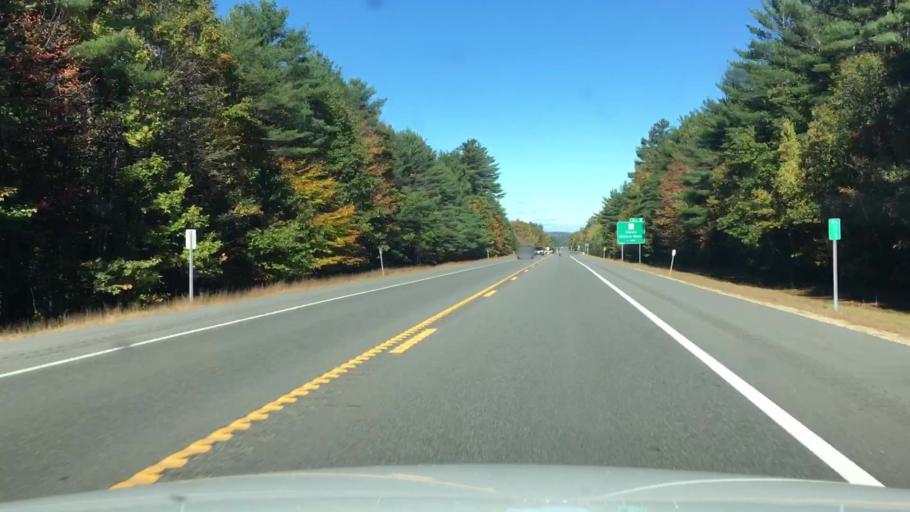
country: US
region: New Hampshire
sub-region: Carroll County
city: Sanbornville
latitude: 43.4618
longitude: -70.9959
